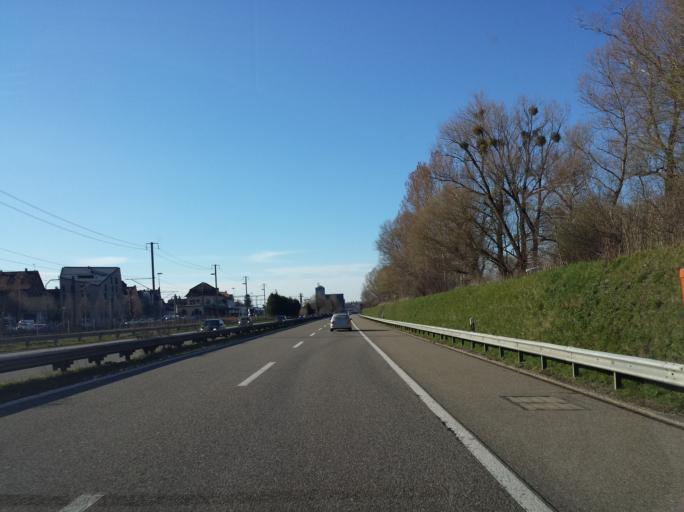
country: CH
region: Saint Gallen
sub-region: Wahlkreis Rheintal
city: Rheineck
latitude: 47.4651
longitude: 9.5929
